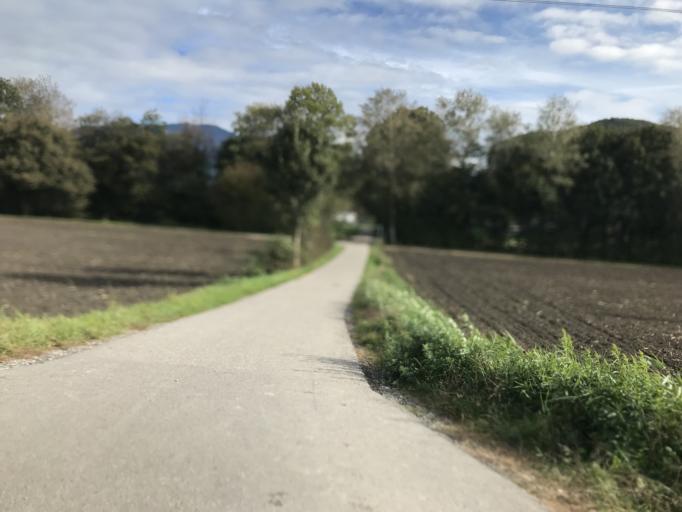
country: AT
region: Vorarlberg
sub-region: Politischer Bezirk Feldkirch
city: Mader
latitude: 47.3472
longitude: 9.6034
